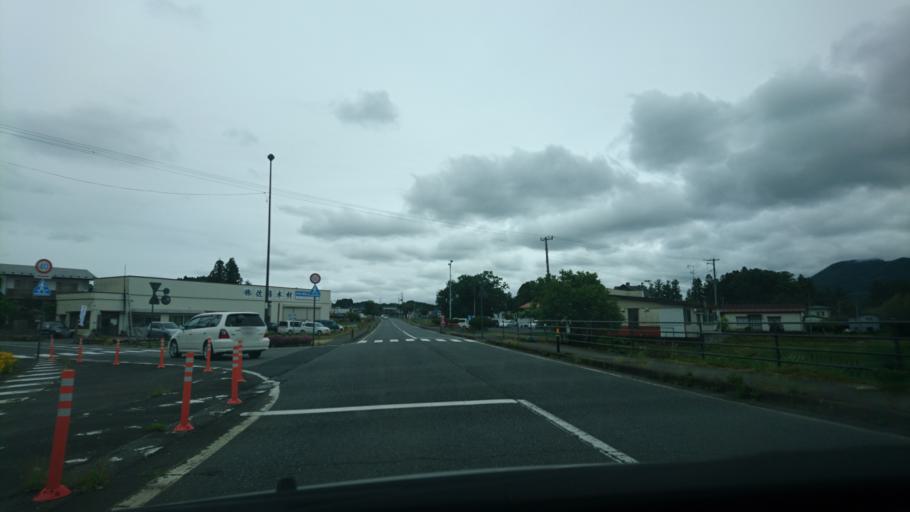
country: JP
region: Iwate
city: Ichinoseki
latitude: 39.0105
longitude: 141.1098
